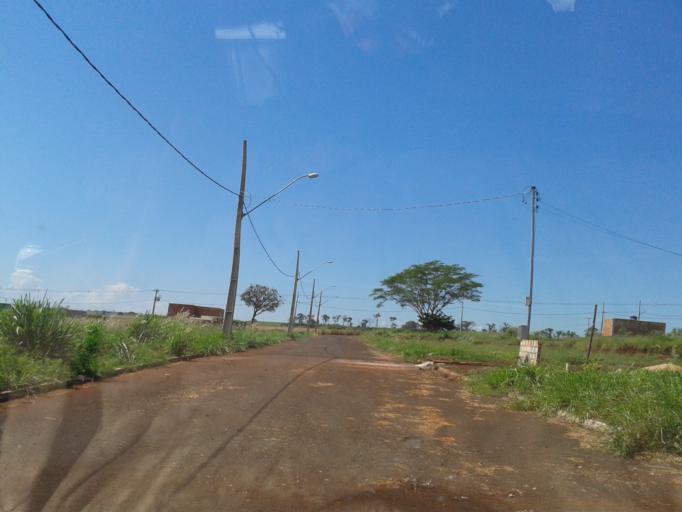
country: BR
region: Goias
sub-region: Itumbiara
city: Itumbiara
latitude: -18.4254
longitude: -49.1824
